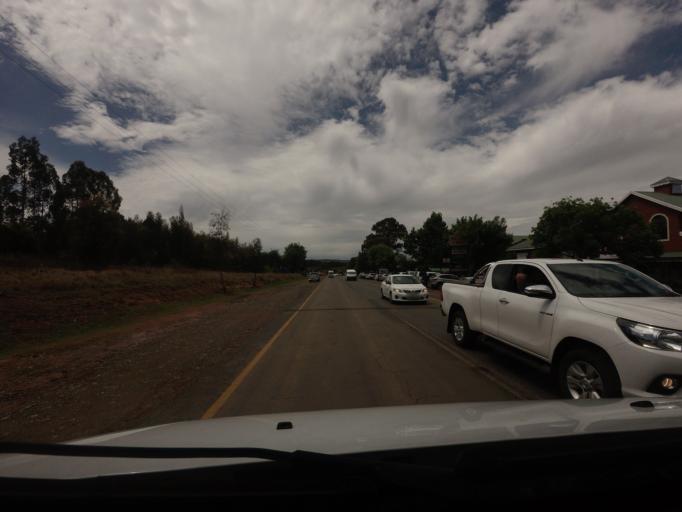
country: ZA
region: Mpumalanga
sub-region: Nkangala District Municipality
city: Belfast
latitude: -25.4192
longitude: 30.1053
